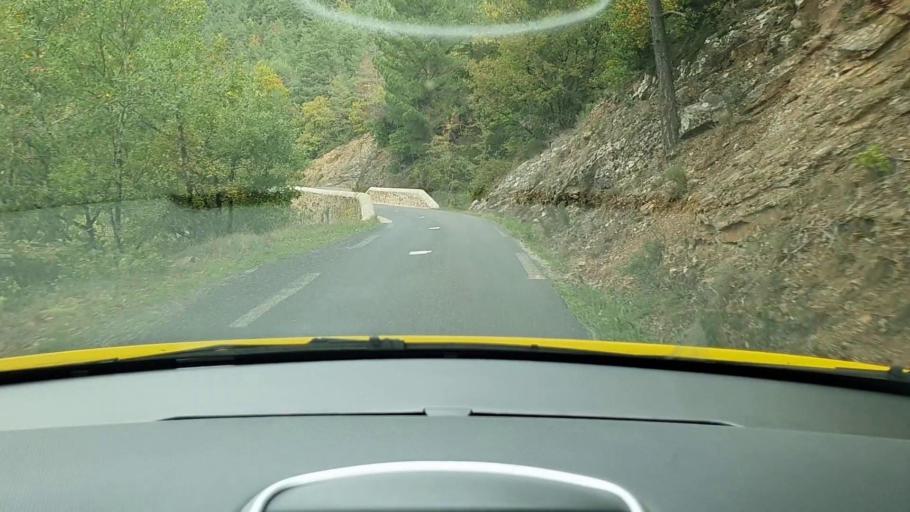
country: FR
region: Languedoc-Roussillon
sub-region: Departement de la Lozere
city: Meyrueis
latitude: 44.1128
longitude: 3.4270
